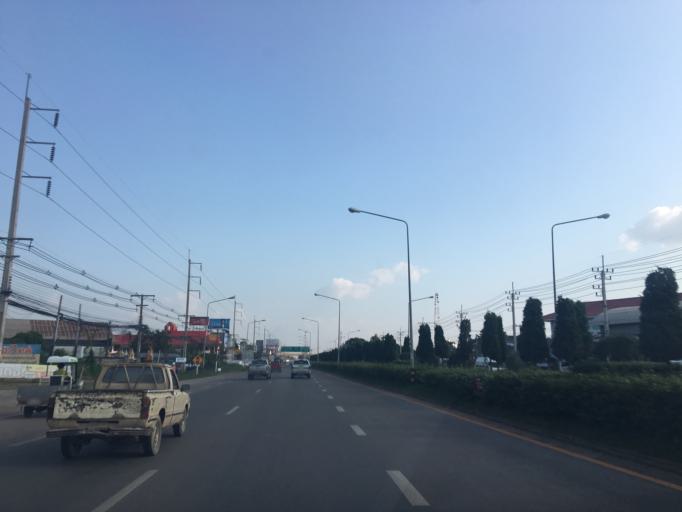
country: TH
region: Phayao
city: Phayao
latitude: 19.1759
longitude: 99.9028
